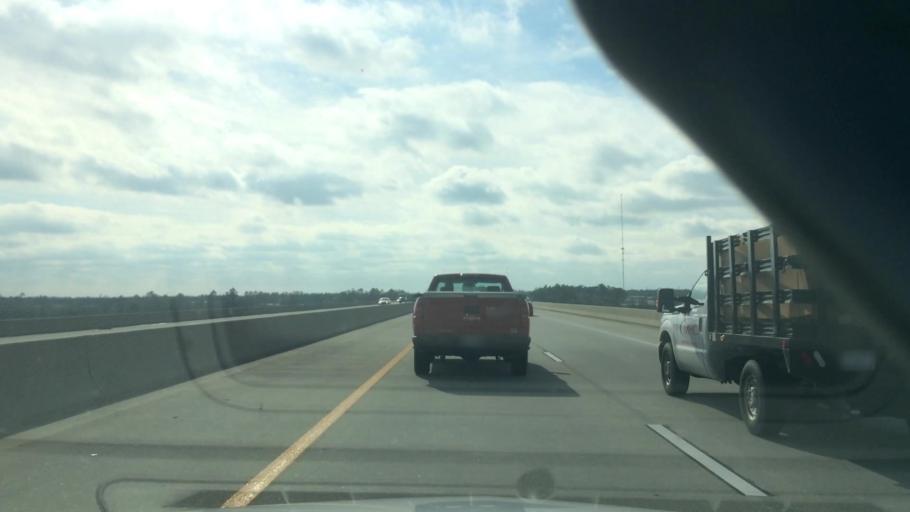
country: US
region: North Carolina
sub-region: New Hanover County
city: Wrightsboro
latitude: 34.2943
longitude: -77.9639
